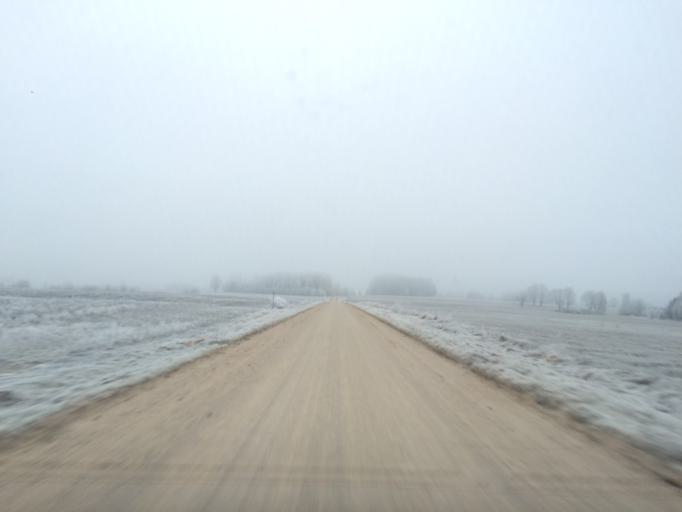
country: LV
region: Ludzas Rajons
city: Ludza
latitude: 56.5956
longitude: 27.5254
